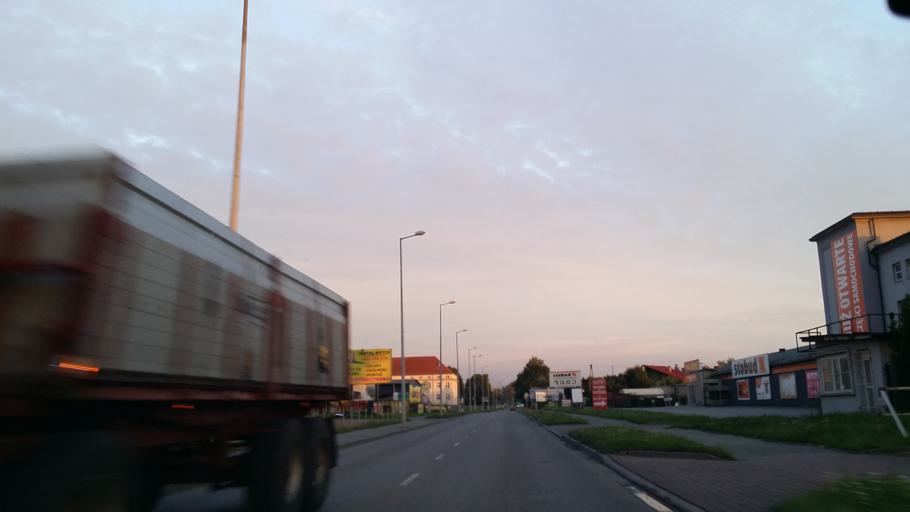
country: PL
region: Lesser Poland Voivodeship
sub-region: Powiat oswiecimski
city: Brzezinka
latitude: 50.0291
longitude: 19.1958
